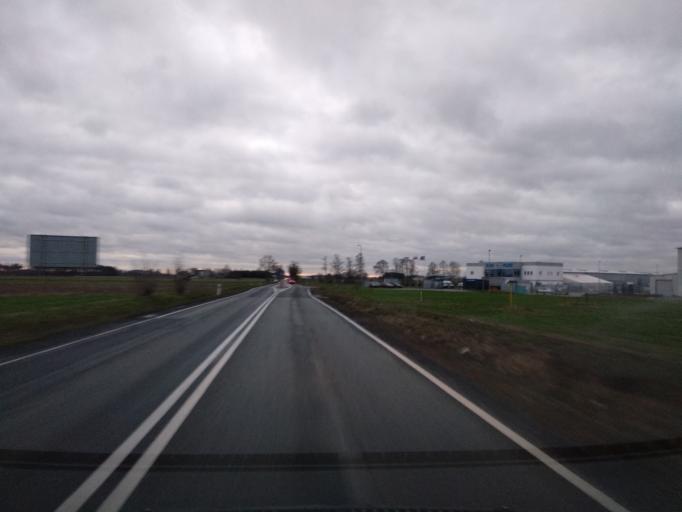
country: PL
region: Greater Poland Voivodeship
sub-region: Powiat koninski
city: Stare Miasto
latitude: 52.1483
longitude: 18.2002
